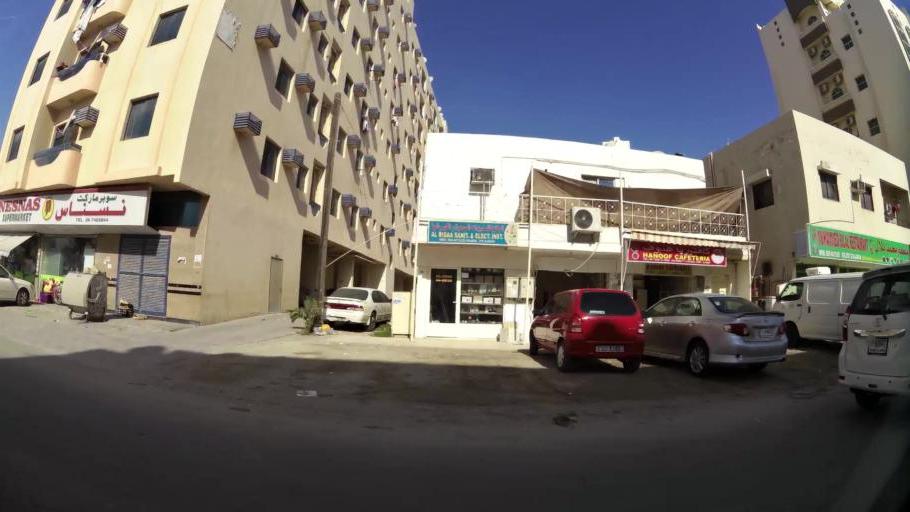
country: AE
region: Ajman
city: Ajman
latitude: 25.4184
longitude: 55.4507
